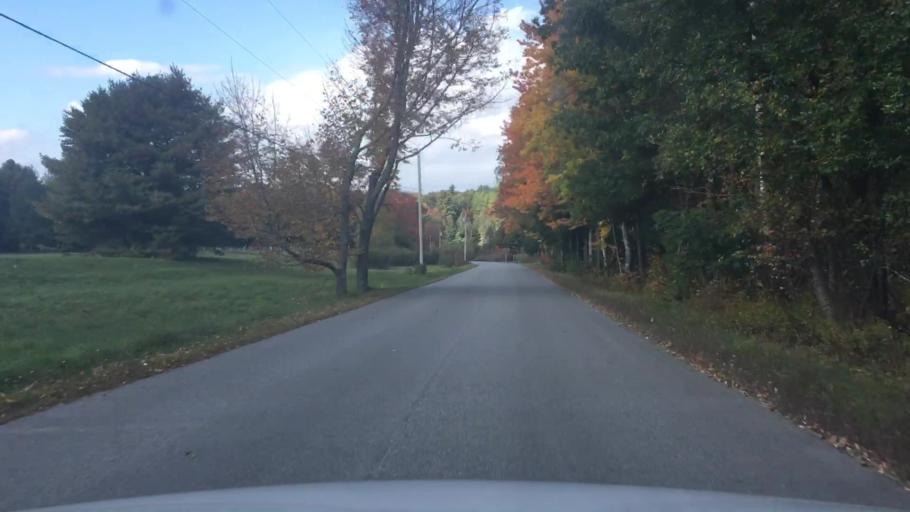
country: US
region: Maine
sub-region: Knox County
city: Washington
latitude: 44.3572
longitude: -69.3925
